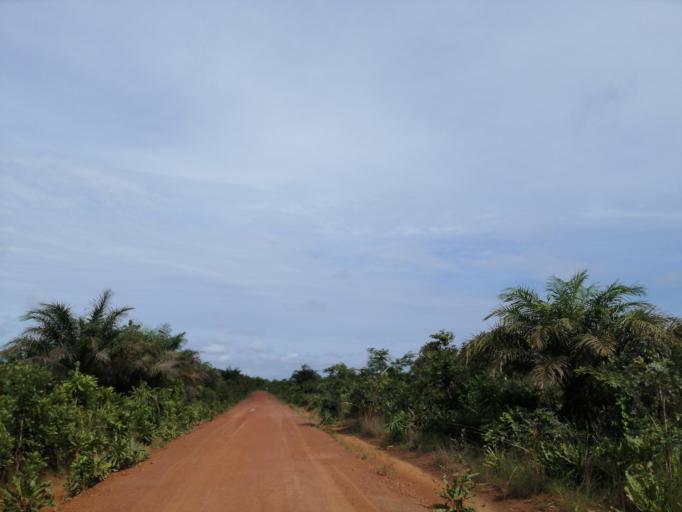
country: SL
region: Northern Province
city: Port Loko
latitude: 8.7691
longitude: -12.9097
